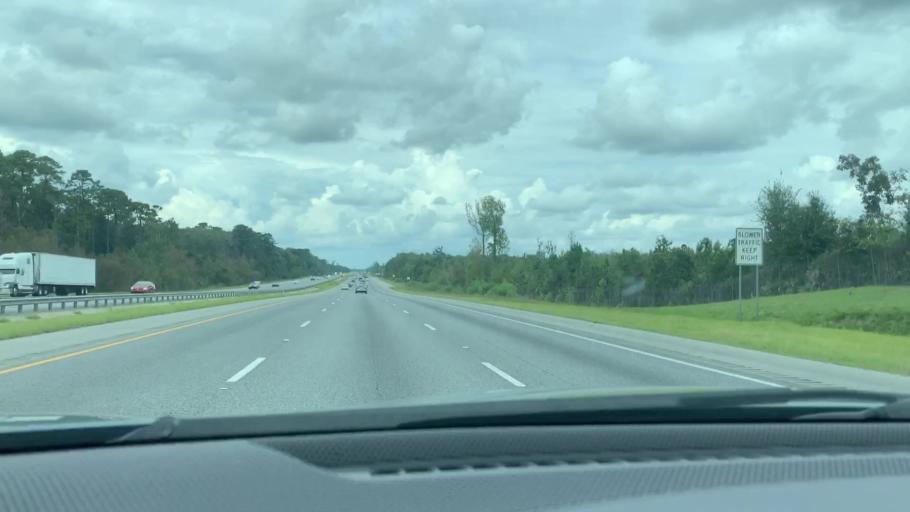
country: US
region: Georgia
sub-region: McIntosh County
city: Darien
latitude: 31.4356
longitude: -81.4439
